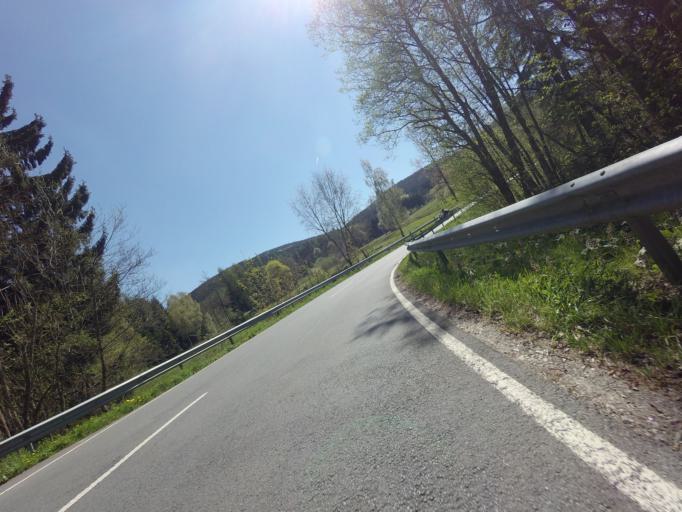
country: DE
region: North Rhine-Westphalia
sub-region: Regierungsbezirk Arnsberg
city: Kirchhundem
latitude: 51.0822
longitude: 8.1824
